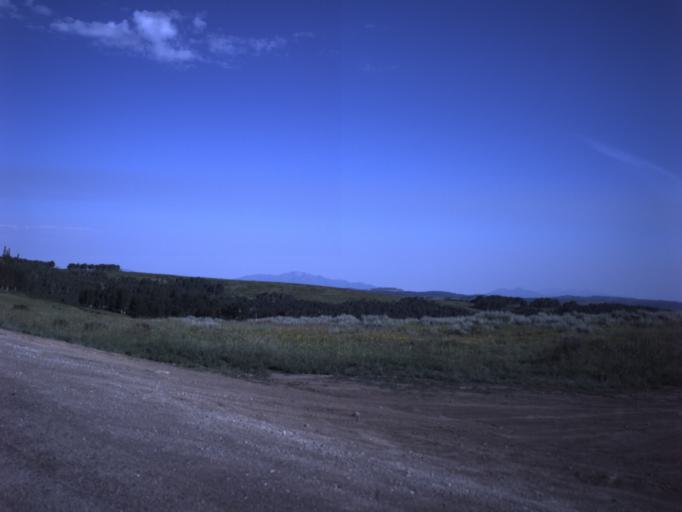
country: US
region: Utah
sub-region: Sanpete County
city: Fairview
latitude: 39.6198
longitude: -111.2873
